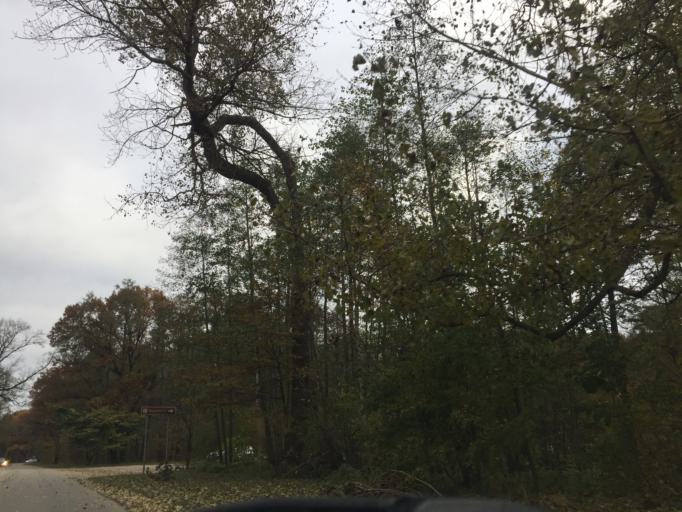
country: LV
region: Liepaja
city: Vec-Liepaja
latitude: 56.5425
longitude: 21.0790
